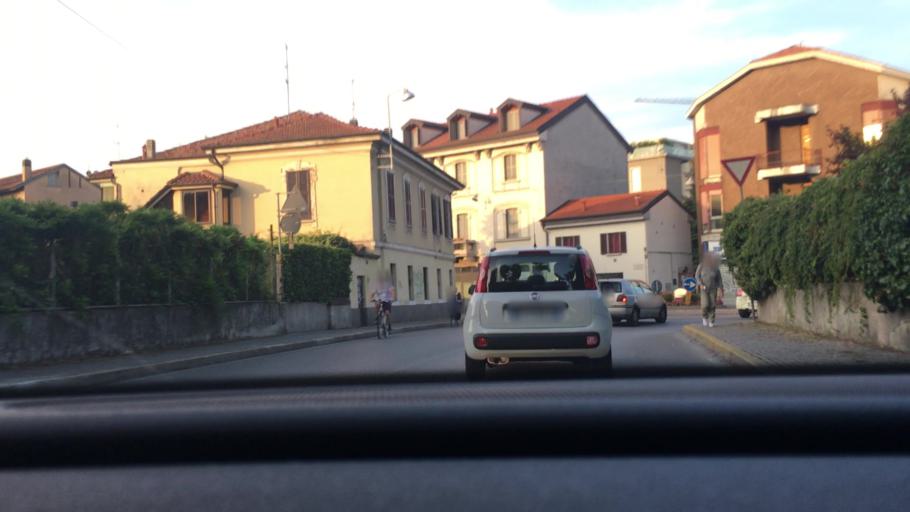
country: IT
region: Lombardy
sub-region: Provincia di Monza e Brianza
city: Monza
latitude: 45.5868
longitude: 9.2656
